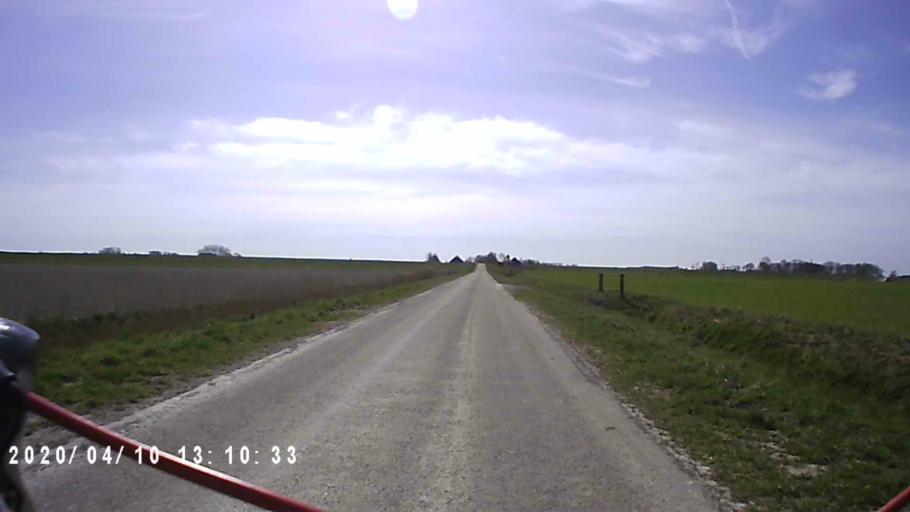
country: NL
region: Groningen
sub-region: Gemeente De Marne
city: Ulrum
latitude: 53.4093
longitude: 6.4191
